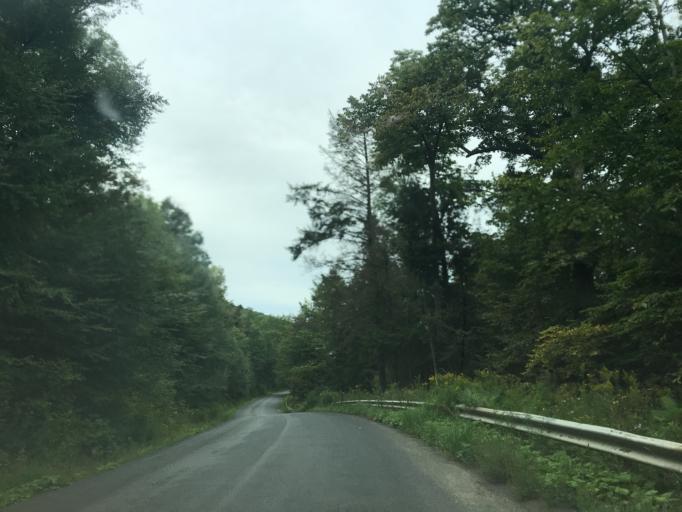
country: US
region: New York
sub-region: Otsego County
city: Worcester
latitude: 42.5905
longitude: -74.7083
